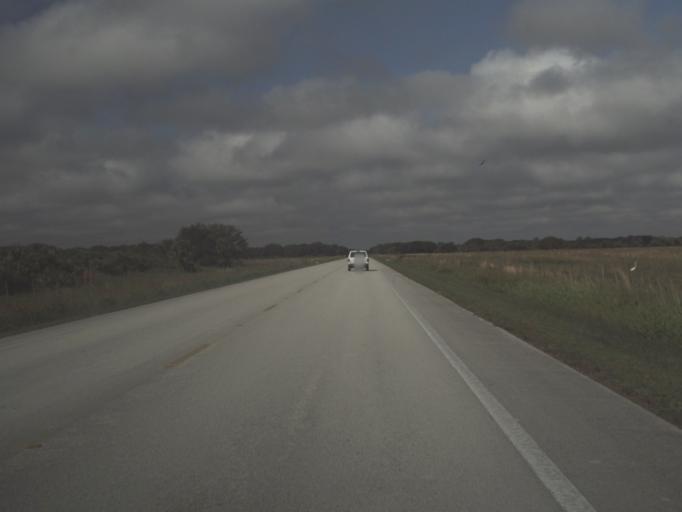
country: US
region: Florida
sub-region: Sarasota County
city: Warm Mineral Springs
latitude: 27.1935
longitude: -82.1689
